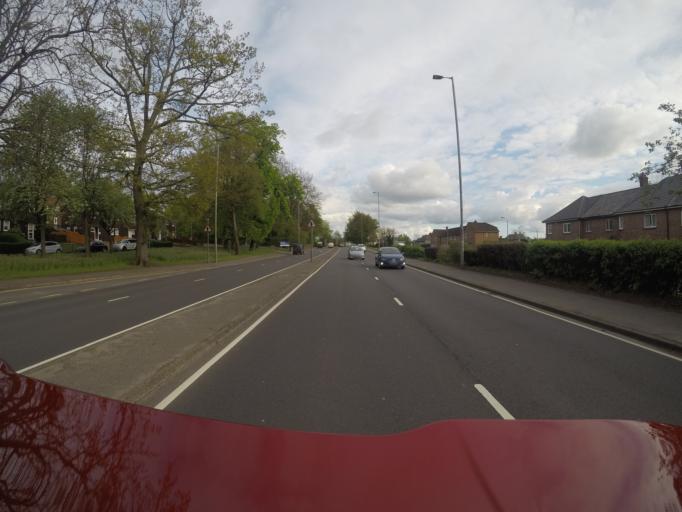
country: GB
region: Scotland
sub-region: West Dunbartonshire
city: Dumbarton
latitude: 55.9458
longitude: -4.5462
